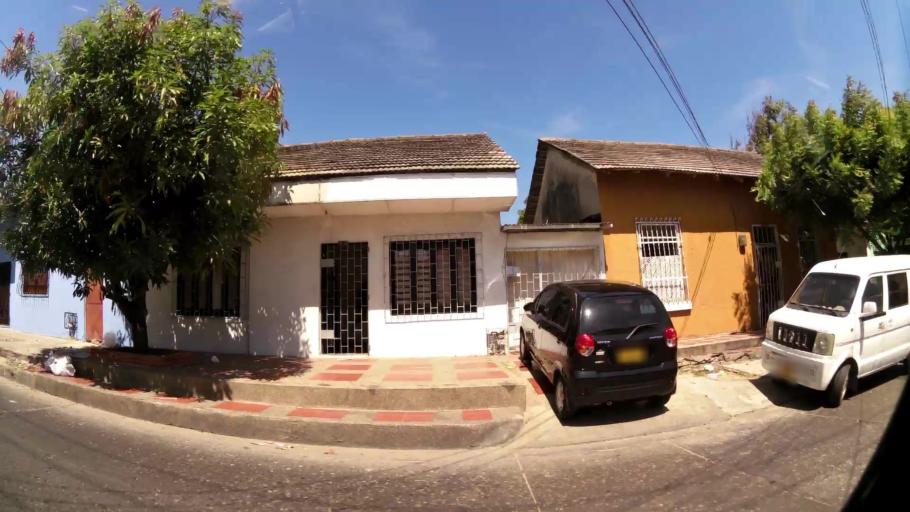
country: CO
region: Atlantico
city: Barranquilla
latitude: 10.9764
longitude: -74.7922
